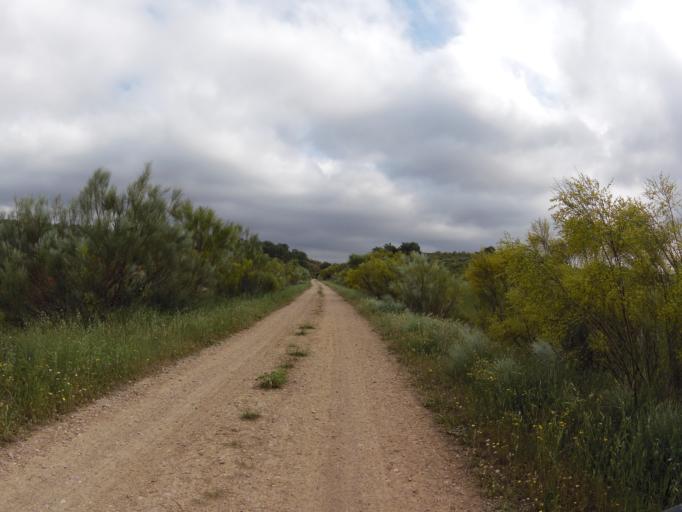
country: ES
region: Castille-La Mancha
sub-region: Provincia de Albacete
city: Robledo
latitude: 38.7234
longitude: -2.4791
